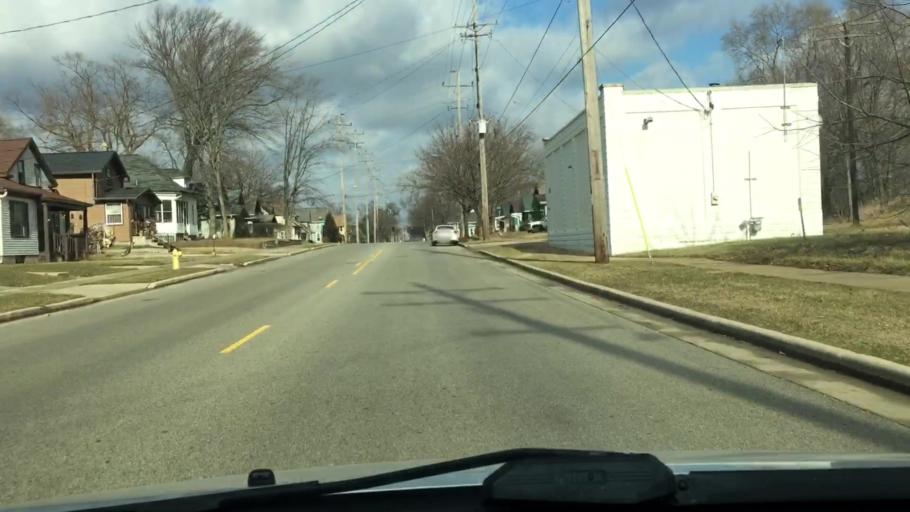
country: US
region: Wisconsin
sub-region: Waukesha County
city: Waukesha
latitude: 43.0004
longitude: -88.2368
